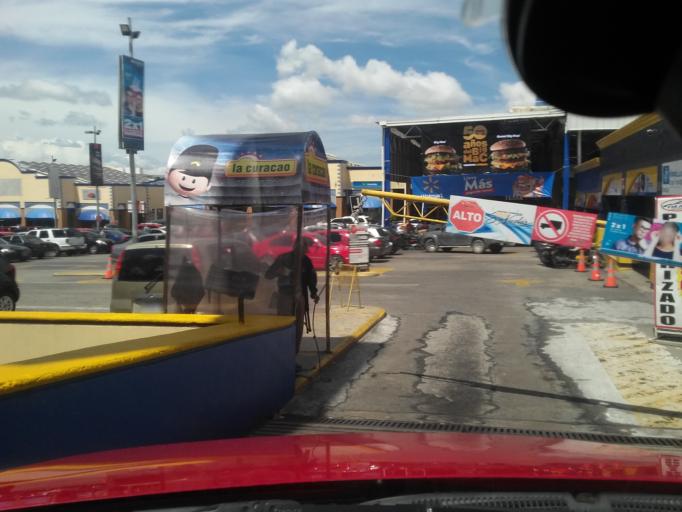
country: GT
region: Guatemala
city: Mixco
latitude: 14.6512
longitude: -90.5680
